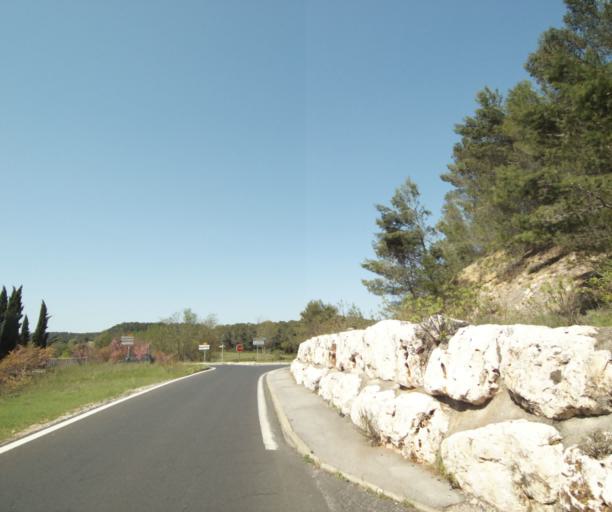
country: FR
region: Languedoc-Roussillon
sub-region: Departement de l'Herault
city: Montferrier-sur-Lez
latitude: 43.6546
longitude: 3.8353
